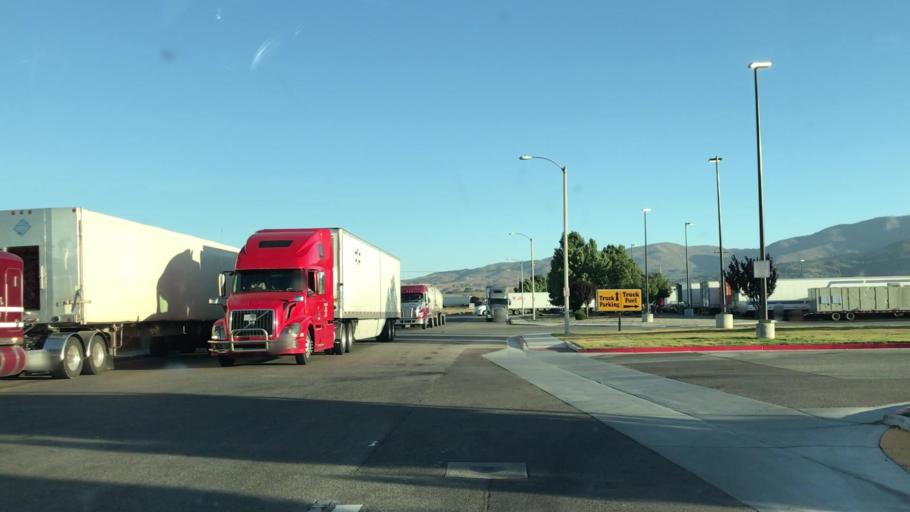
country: US
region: California
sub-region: Kern County
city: Tehachapi
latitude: 35.1261
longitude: -118.4071
